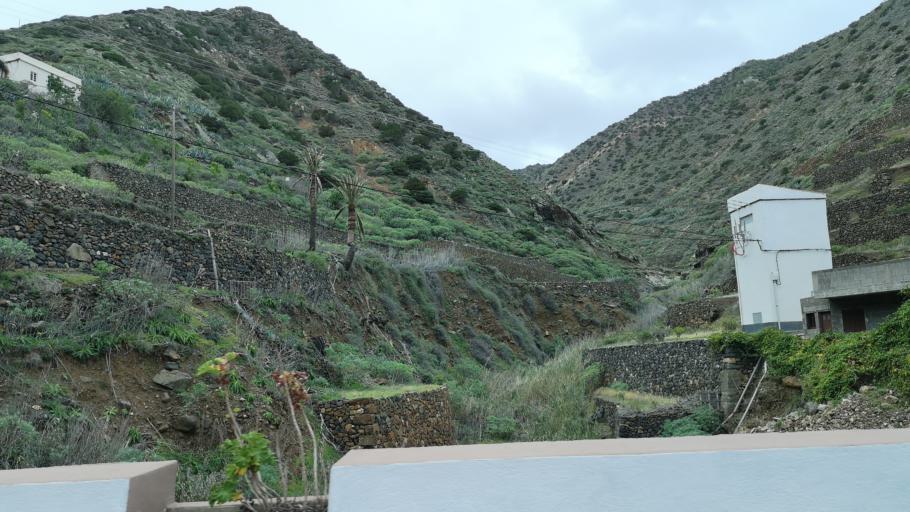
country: ES
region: Canary Islands
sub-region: Provincia de Santa Cruz de Tenerife
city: Vallehermosa
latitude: 28.1986
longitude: -17.2563
